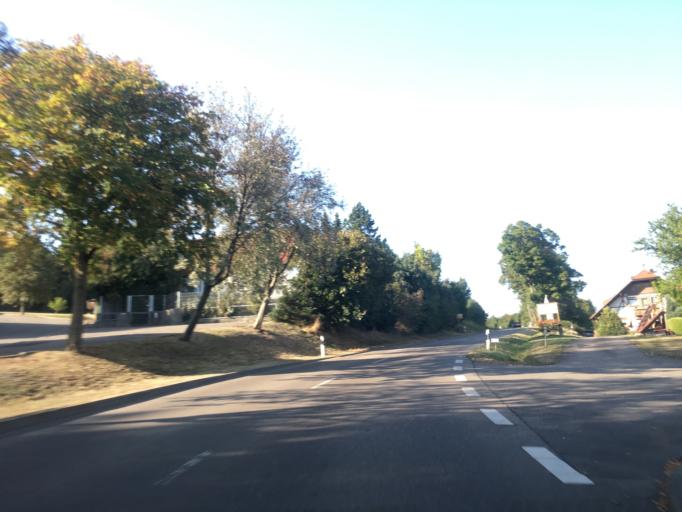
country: DE
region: Baden-Wuerttemberg
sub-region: Tuebingen Region
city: Hayingen
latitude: 48.2773
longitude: 9.4735
